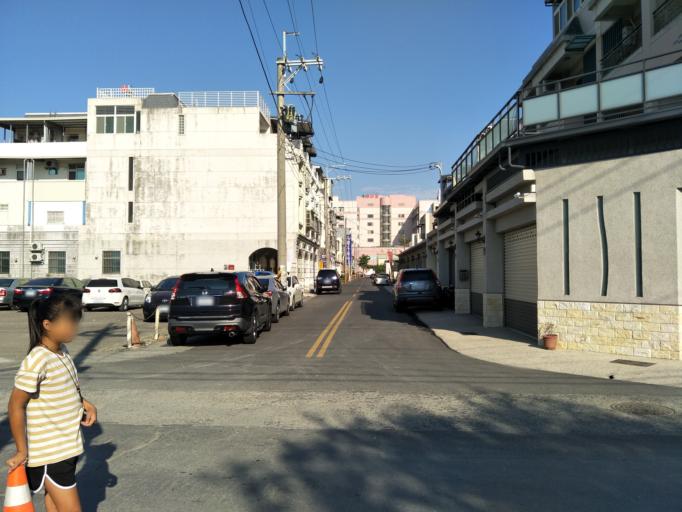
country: TW
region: Taiwan
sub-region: Changhua
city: Chang-hua
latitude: 23.9508
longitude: 120.5245
